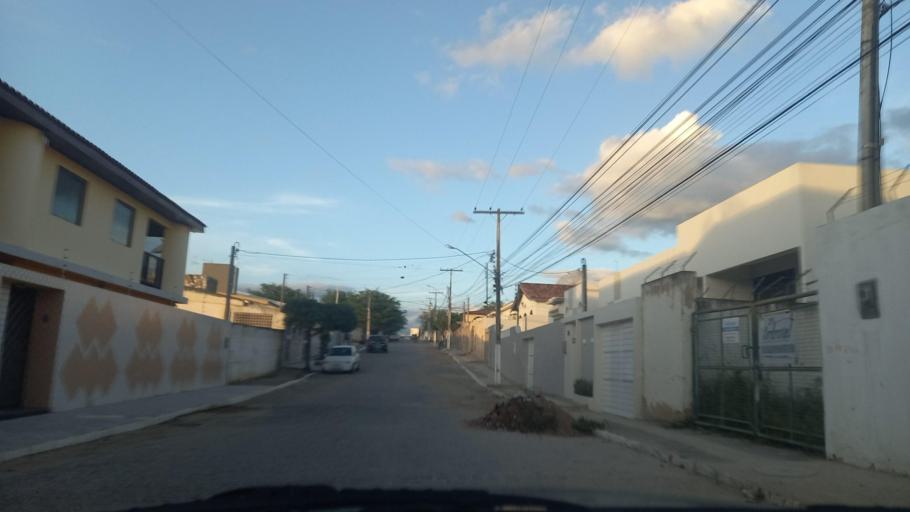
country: BR
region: Pernambuco
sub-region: Bezerros
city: Bezerros
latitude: -8.2383
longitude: -35.7492
